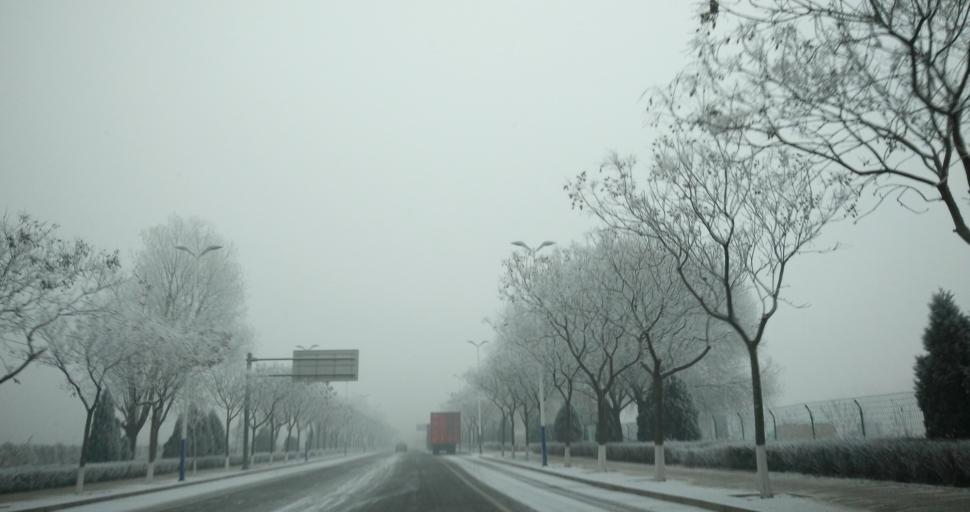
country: CN
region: Beijing
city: Yinghai
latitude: 39.7002
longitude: 116.4114
